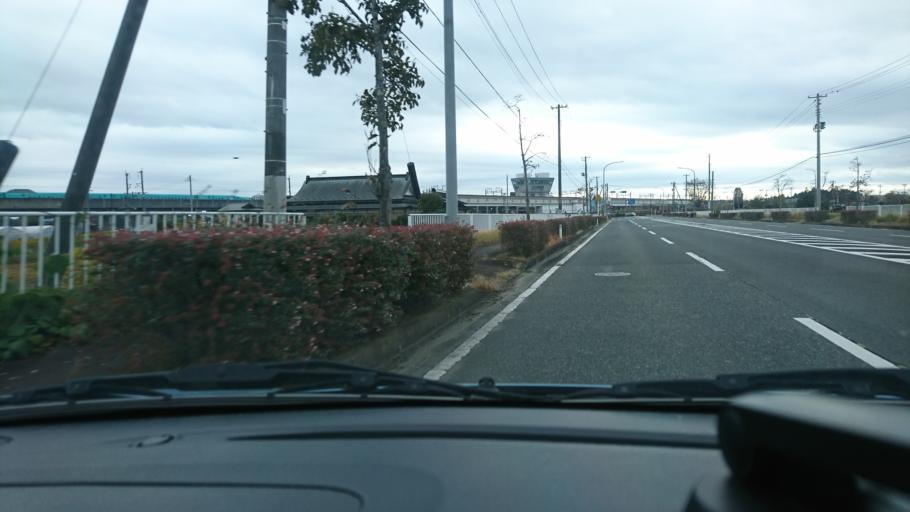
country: JP
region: Iwate
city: Ichinoseki
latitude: 38.7526
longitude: 141.0715
